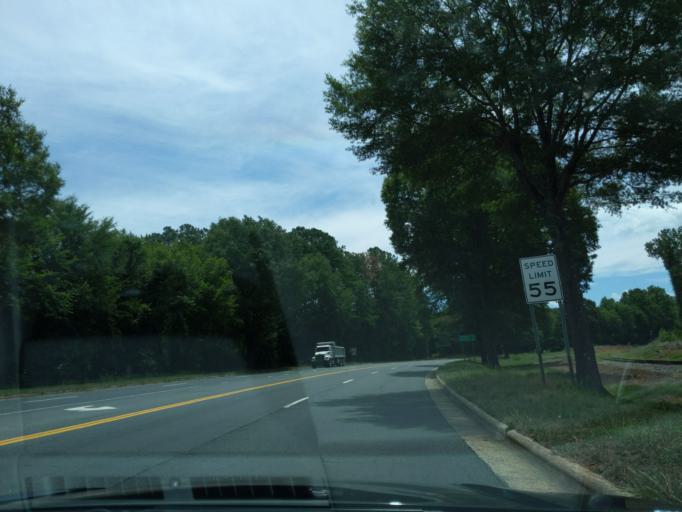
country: US
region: North Carolina
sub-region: Stanly County
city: Albemarle
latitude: 35.4439
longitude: -80.2232
